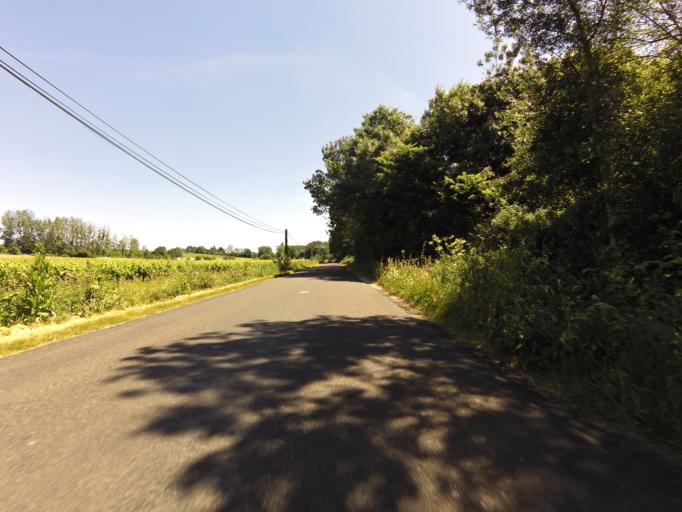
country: FR
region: Pays de la Loire
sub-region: Departement de la Loire-Atlantique
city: Le Loroux-Bottereau
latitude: 47.2104
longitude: -1.3604
